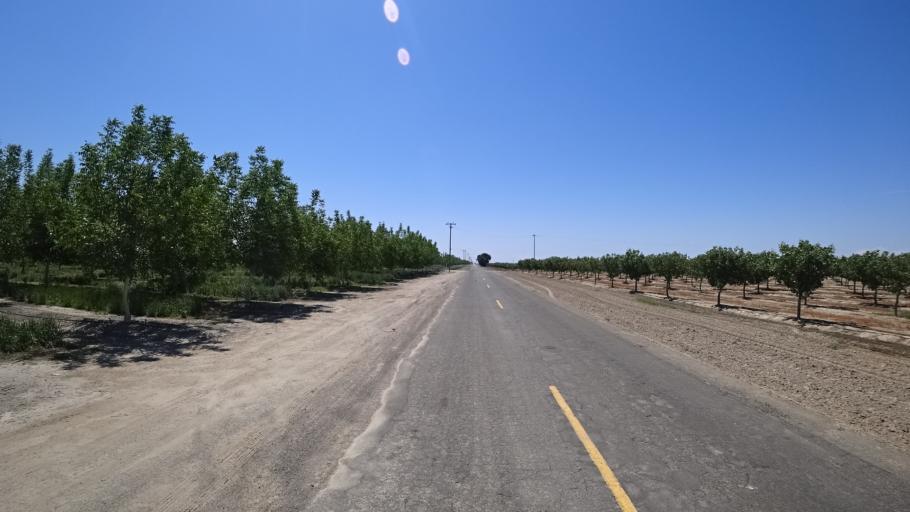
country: US
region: California
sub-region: Kings County
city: Armona
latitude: 36.2483
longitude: -119.7268
